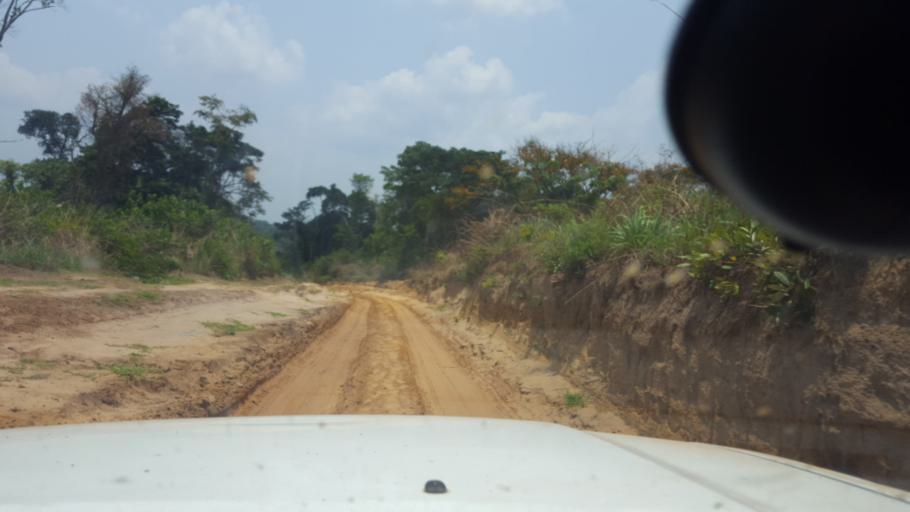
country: CD
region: Bandundu
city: Mushie
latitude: -3.7555
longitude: 16.6264
